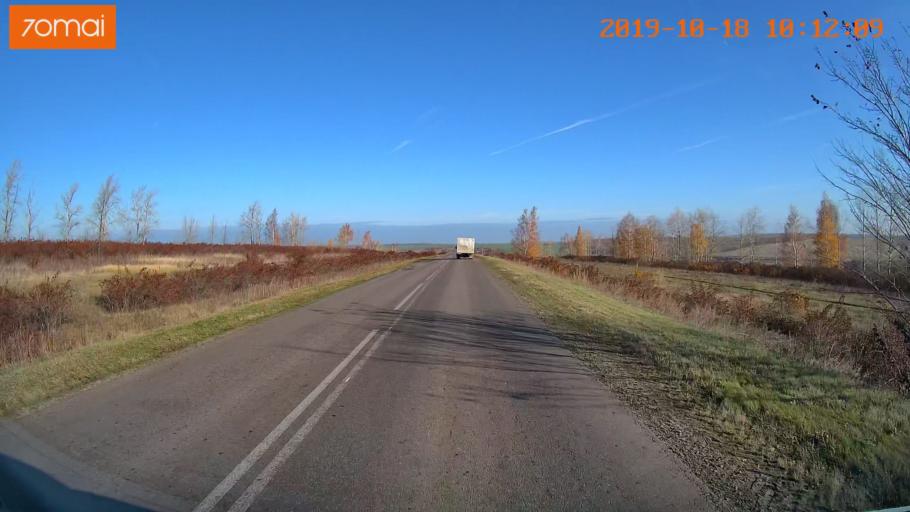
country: RU
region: Tula
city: Kurkino
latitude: 53.3907
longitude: 38.5055
